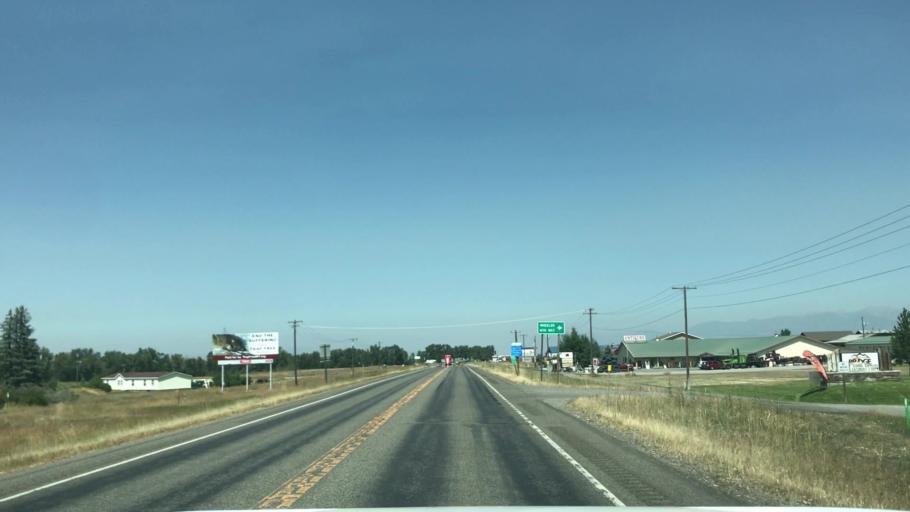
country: US
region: Montana
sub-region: Gallatin County
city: Four Corners
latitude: 45.6013
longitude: -111.1962
